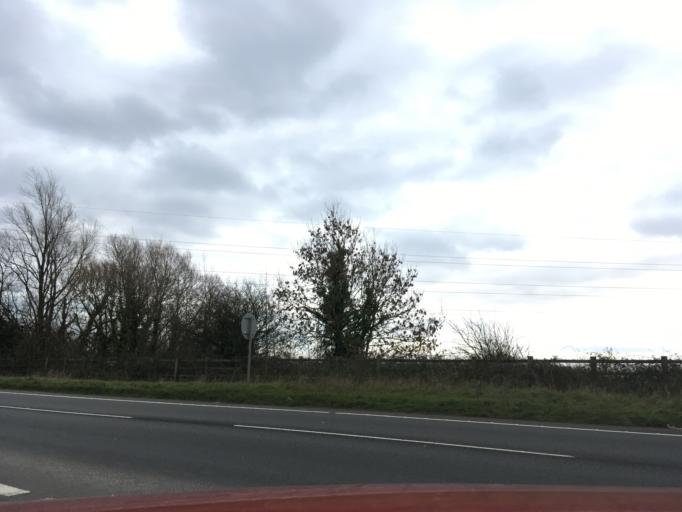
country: GB
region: Wales
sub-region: Monmouthshire
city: Magor
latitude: 51.5753
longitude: -2.8492
